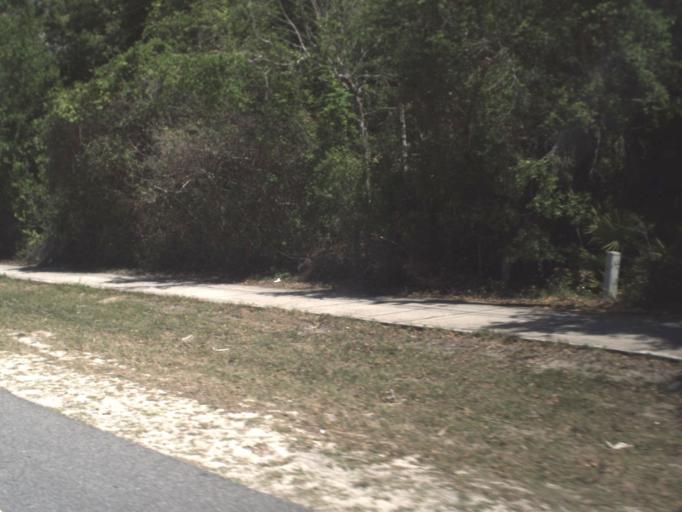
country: US
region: Florida
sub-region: Flagler County
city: Palm Coast
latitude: 29.5937
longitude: -81.1943
